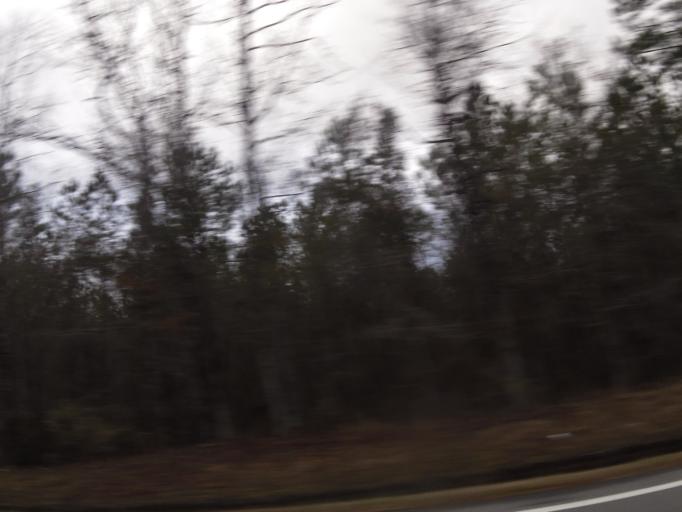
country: US
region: North Carolina
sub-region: Pitt County
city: Greenville
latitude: 35.6871
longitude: -77.3573
